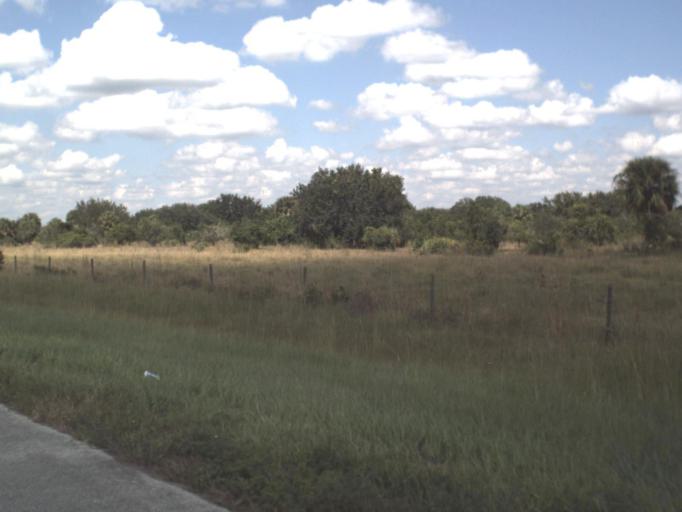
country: US
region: Florida
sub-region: Highlands County
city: Lake Placid
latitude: 27.4188
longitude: -81.2015
